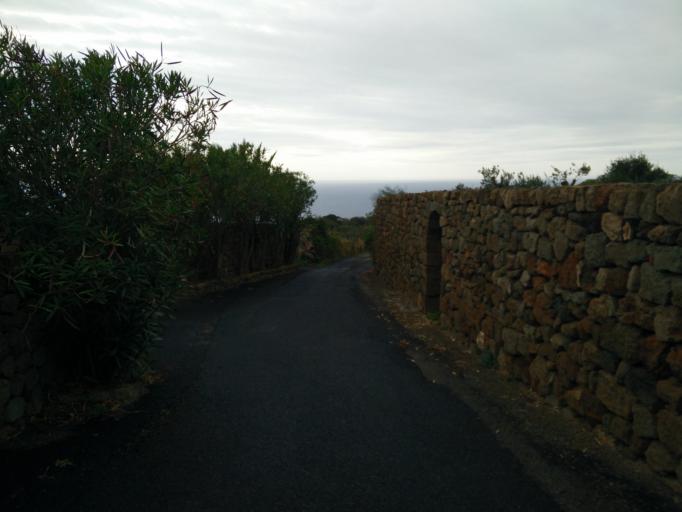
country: IT
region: Sicily
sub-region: Trapani
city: Kamma
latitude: 36.7507
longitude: 11.9975
